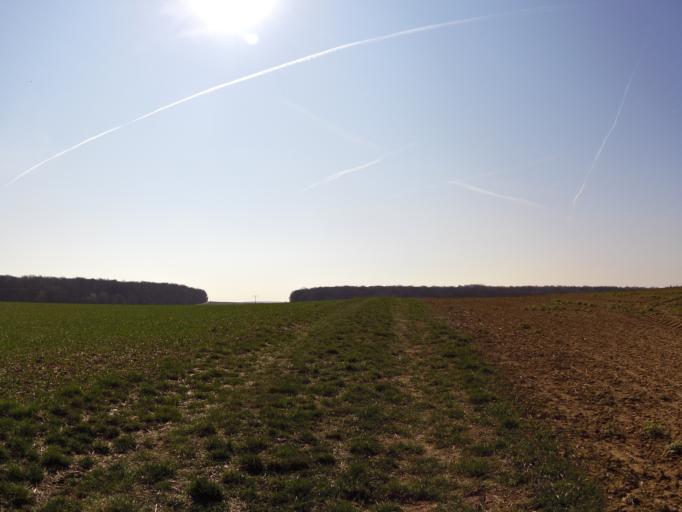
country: DE
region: Bavaria
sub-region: Regierungsbezirk Unterfranken
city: Rottendorf
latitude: 49.8166
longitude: 10.0265
